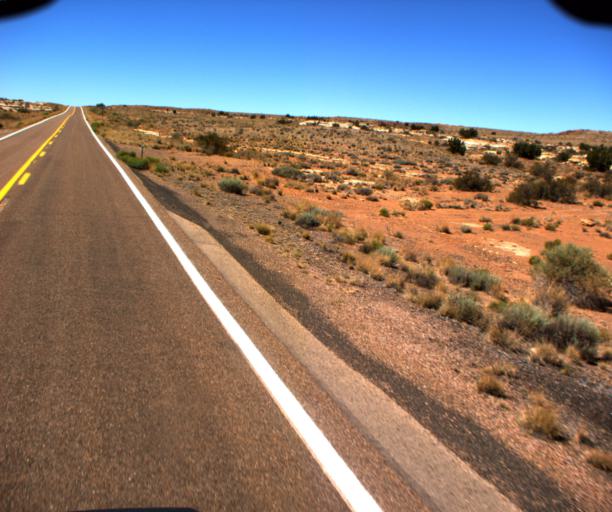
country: US
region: Arizona
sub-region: Navajo County
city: Winslow
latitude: 34.9651
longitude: -110.6468
